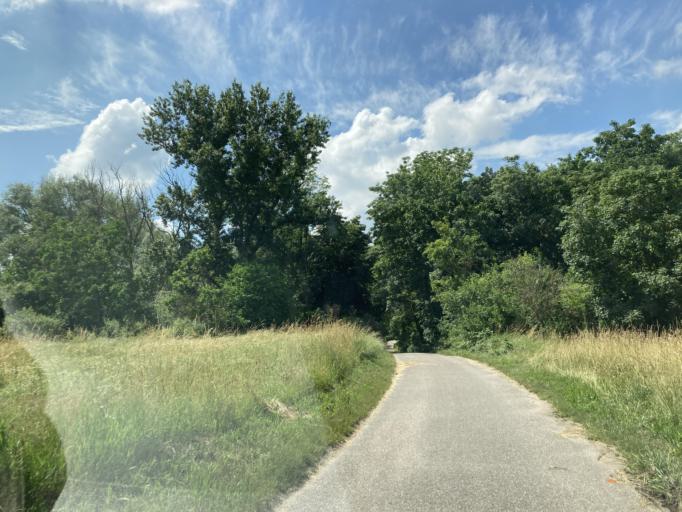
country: DE
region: Baden-Wuerttemberg
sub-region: Karlsruhe Region
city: Oberhausen-Rheinhausen
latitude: 49.2691
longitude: 8.4809
